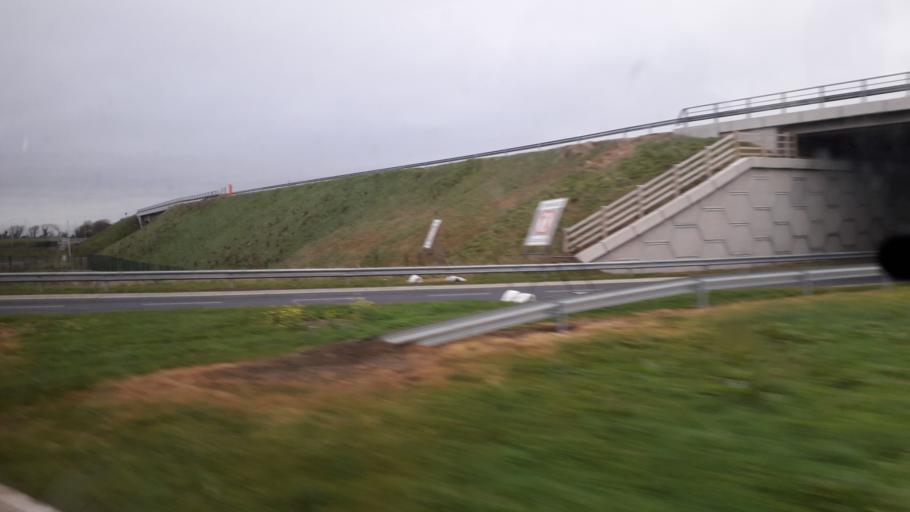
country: IE
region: Connaught
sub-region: County Galway
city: Athenry
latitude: 53.2957
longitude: -8.8087
